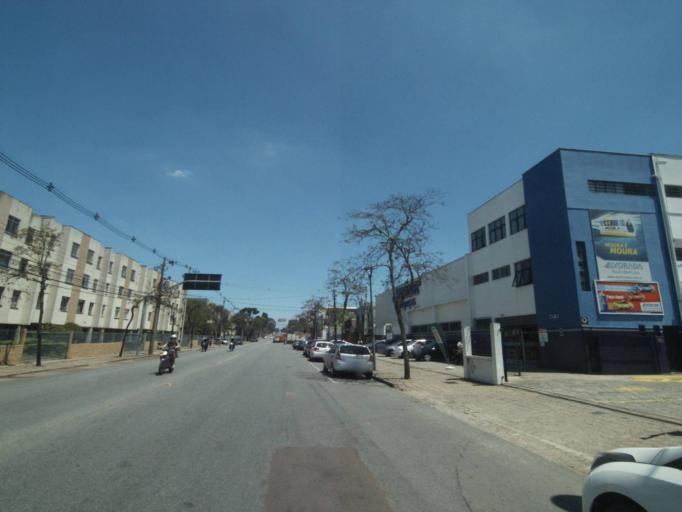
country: BR
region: Parana
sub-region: Curitiba
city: Curitiba
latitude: -25.3915
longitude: -49.2250
